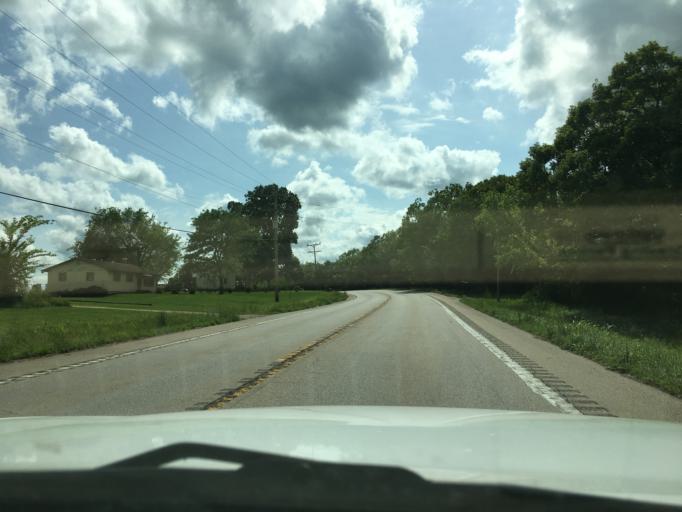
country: US
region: Missouri
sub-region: Franklin County
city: Gerald
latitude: 38.4107
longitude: -91.3151
